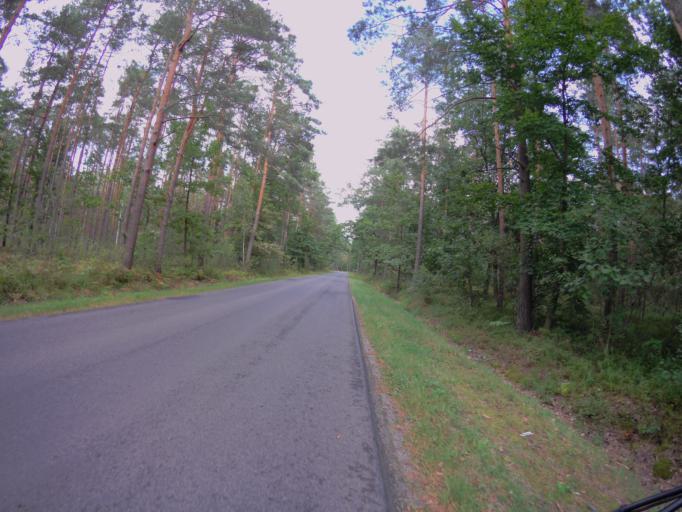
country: PL
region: Subcarpathian Voivodeship
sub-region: Powiat lezajski
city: Brzoza Krolewska
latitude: 50.2440
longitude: 22.3626
